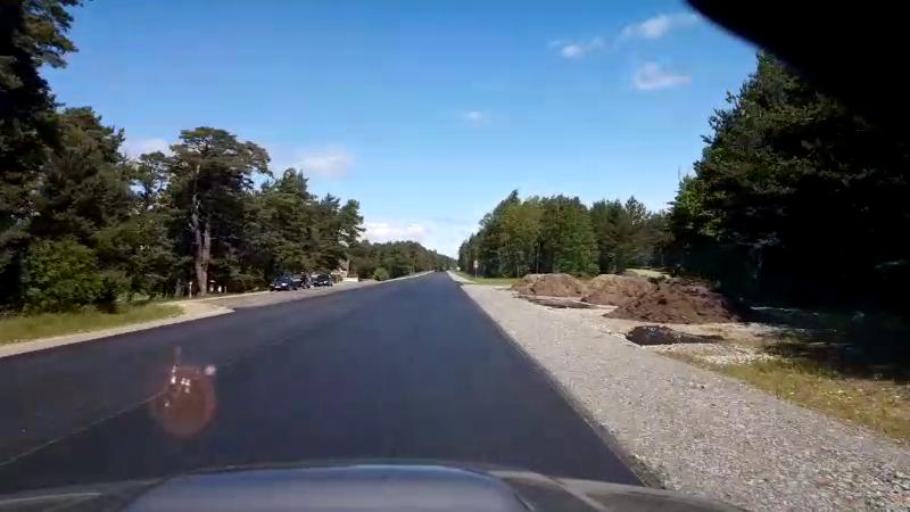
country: LV
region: Salacgrivas
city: Ainazi
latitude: 57.8349
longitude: 24.3456
